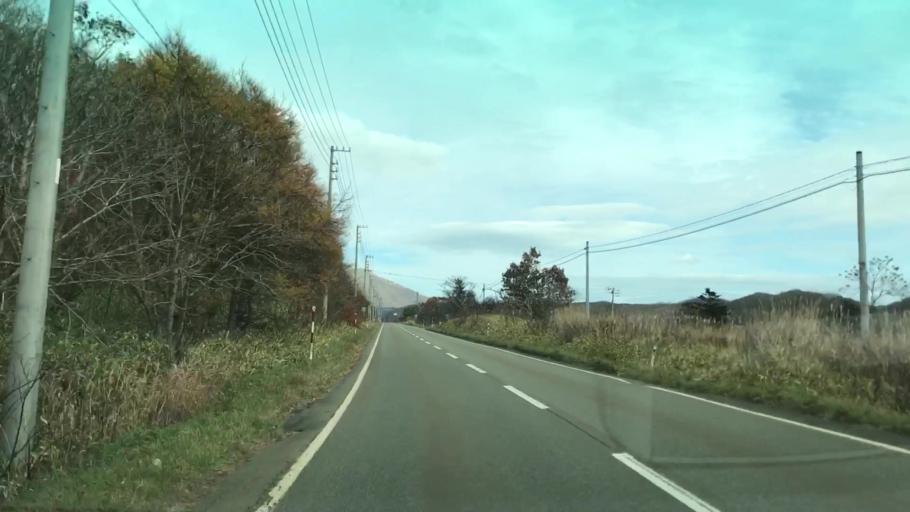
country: JP
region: Hokkaido
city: Shizunai-furukawacho
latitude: 42.0052
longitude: 143.1869
